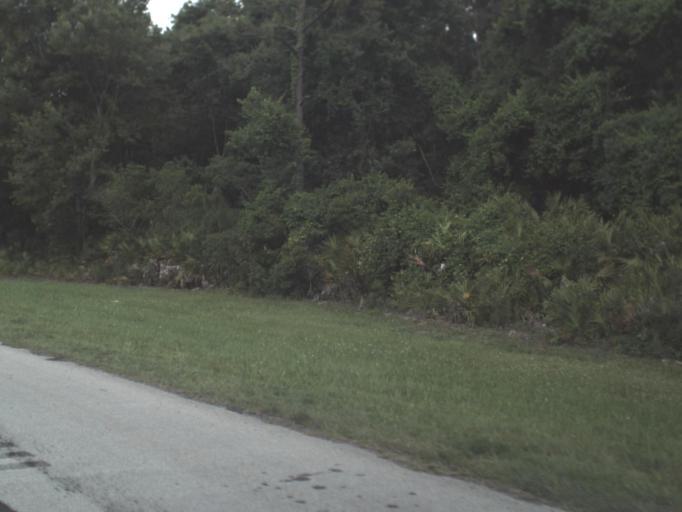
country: US
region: Florida
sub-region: Saint Johns County
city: Saint Augustine
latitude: 29.8999
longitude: -81.4065
